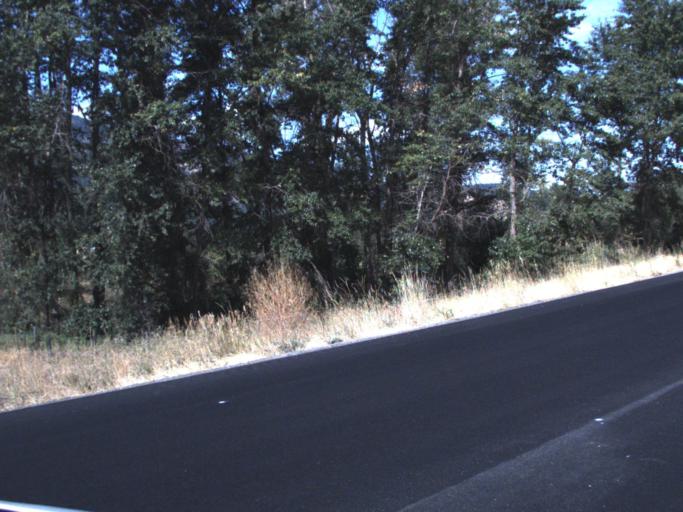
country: US
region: Washington
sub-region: Stevens County
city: Colville
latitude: 48.4858
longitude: -117.9024
